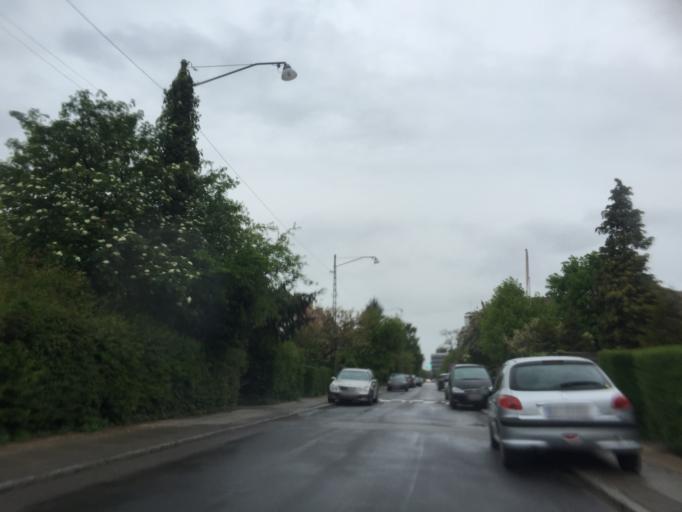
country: DK
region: Capital Region
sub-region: Kobenhavn
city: Vanlose
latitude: 55.6808
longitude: 12.5032
